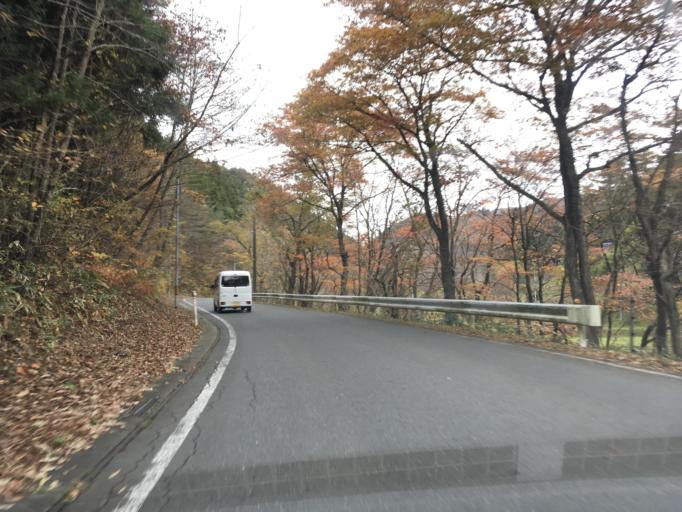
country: JP
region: Iwate
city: Mizusawa
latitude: 39.0988
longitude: 141.3364
